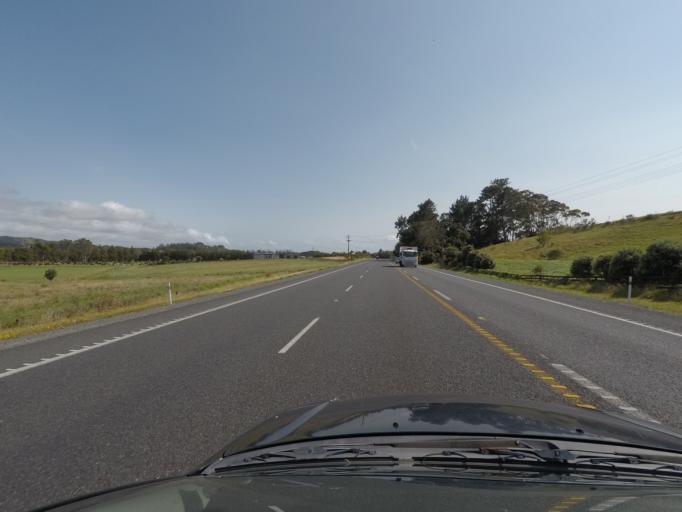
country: NZ
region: Northland
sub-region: Whangarei
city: Ruakaka
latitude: -35.9501
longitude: 174.4537
